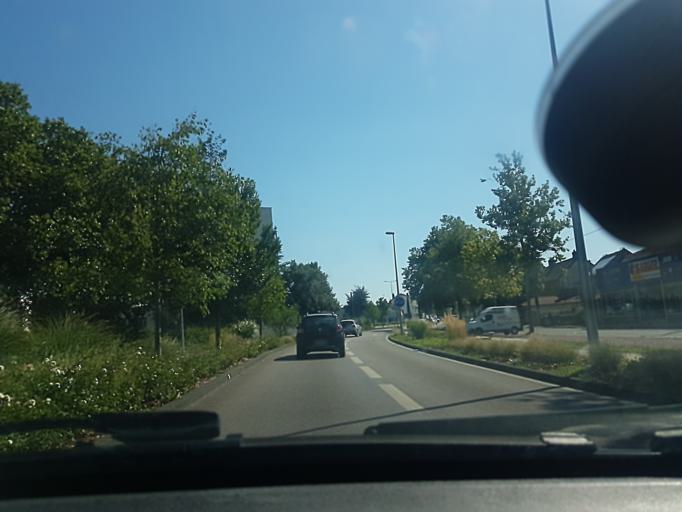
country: FR
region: Bourgogne
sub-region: Departement de Saone-et-Loire
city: Chalon-sur-Saone
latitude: 46.7918
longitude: 4.8632
